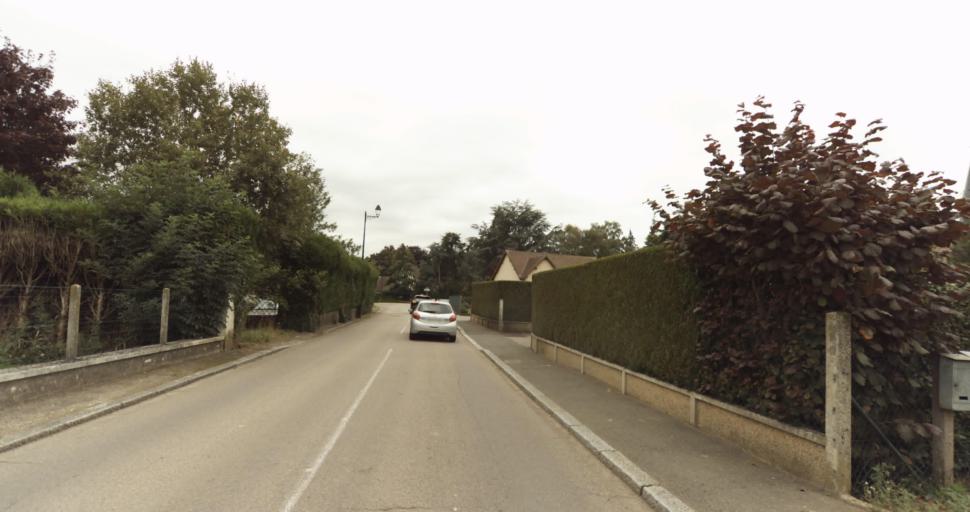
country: FR
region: Haute-Normandie
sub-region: Departement de l'Eure
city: Gravigny
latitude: 49.0384
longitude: 1.2093
